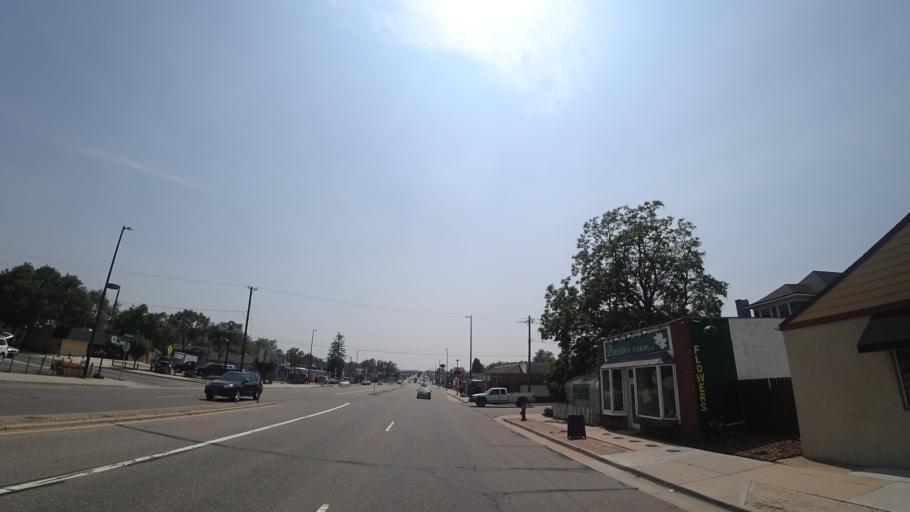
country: US
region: Colorado
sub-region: Arapahoe County
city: Englewood
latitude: 39.6353
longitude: -104.9879
